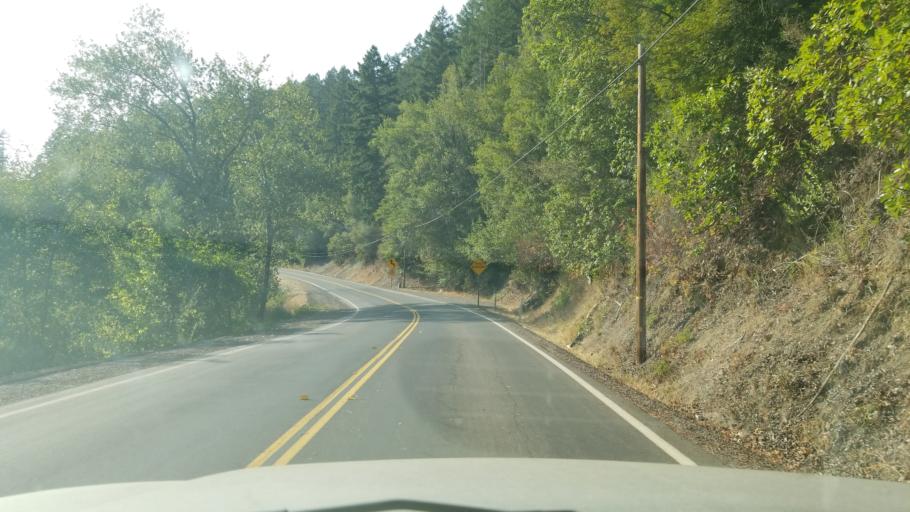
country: US
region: California
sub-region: Humboldt County
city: Redway
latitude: 40.2221
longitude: -123.7884
